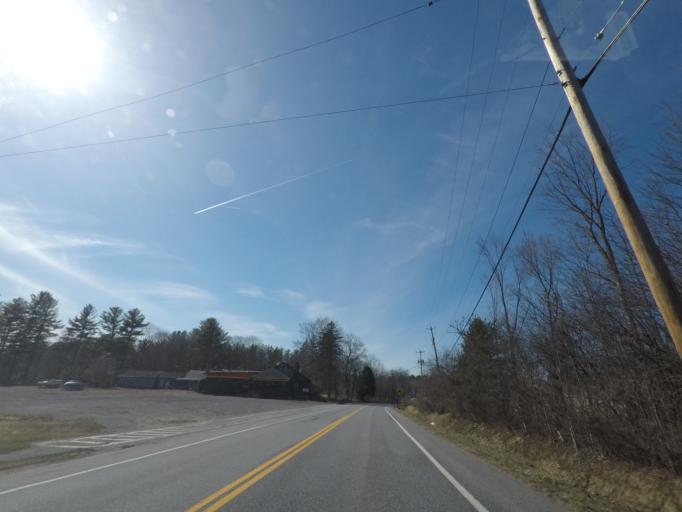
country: US
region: New York
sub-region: Saratoga County
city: Ballston Spa
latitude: 43.0009
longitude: -73.8294
